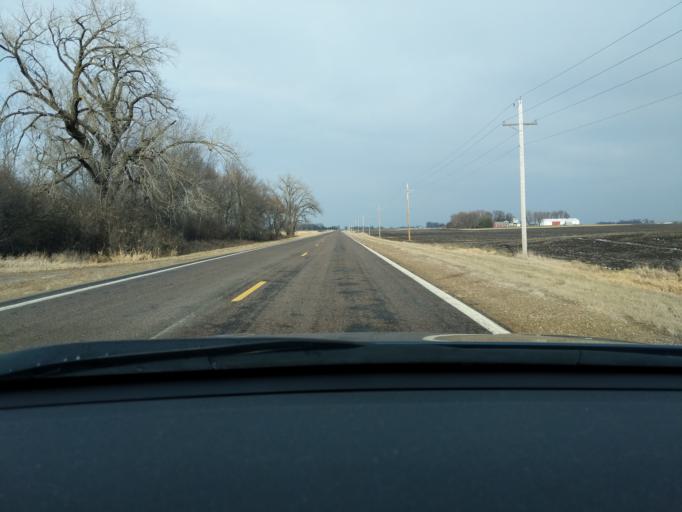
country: US
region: Minnesota
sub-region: Renville County
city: Renville
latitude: 44.7544
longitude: -95.3408
